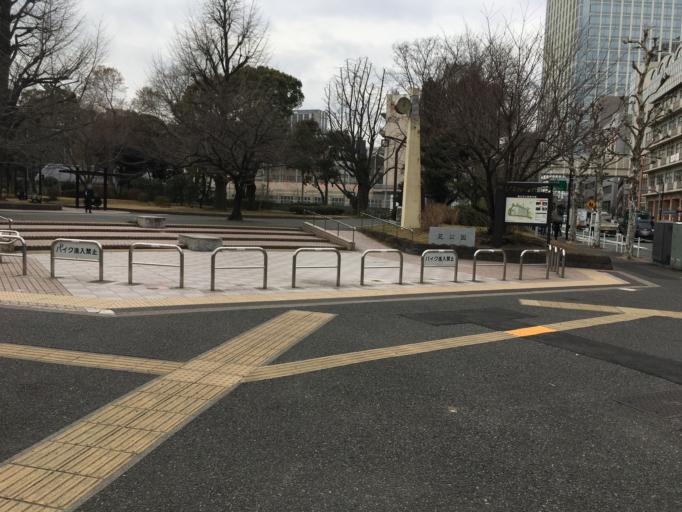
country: JP
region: Tokyo
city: Tokyo
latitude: 35.6610
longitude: 139.7513
